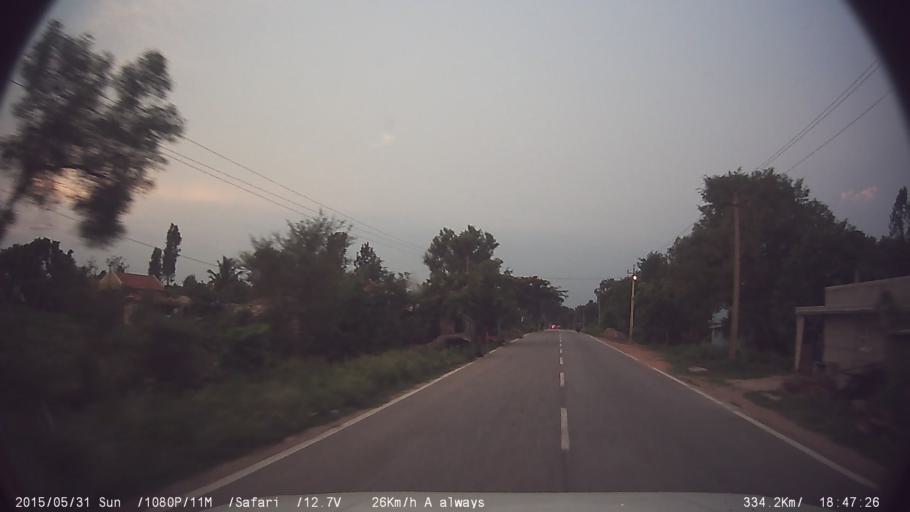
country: IN
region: Karnataka
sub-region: Mysore
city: Tirumakudal Narsipur
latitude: 12.1636
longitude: 76.8409
